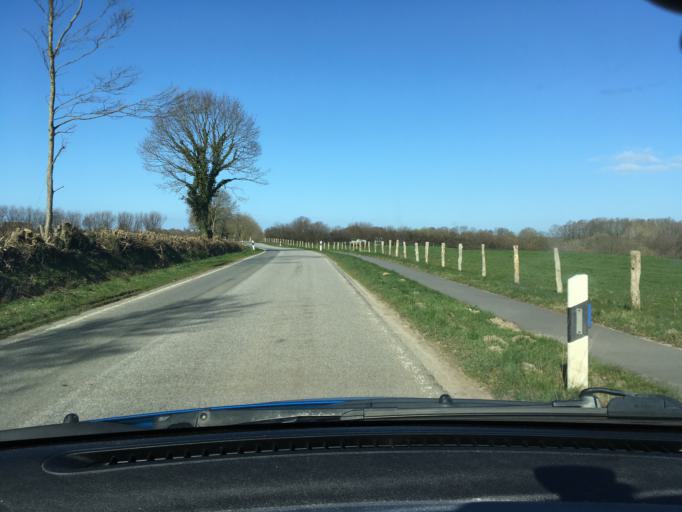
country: DE
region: Schleswig-Holstein
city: Borgwedel
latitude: 54.5015
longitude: 9.6429
